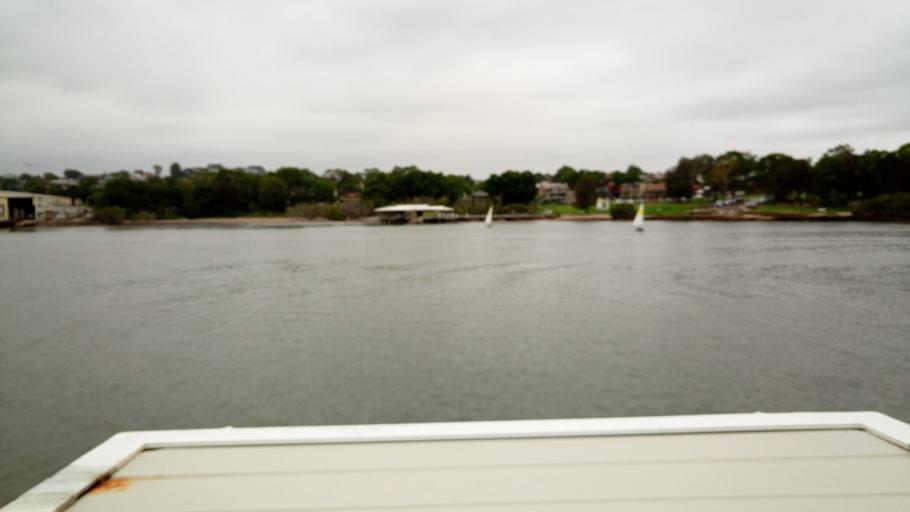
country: AU
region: New South Wales
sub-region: Canada Bay
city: Rhodes
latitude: -33.8293
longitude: 151.0985
